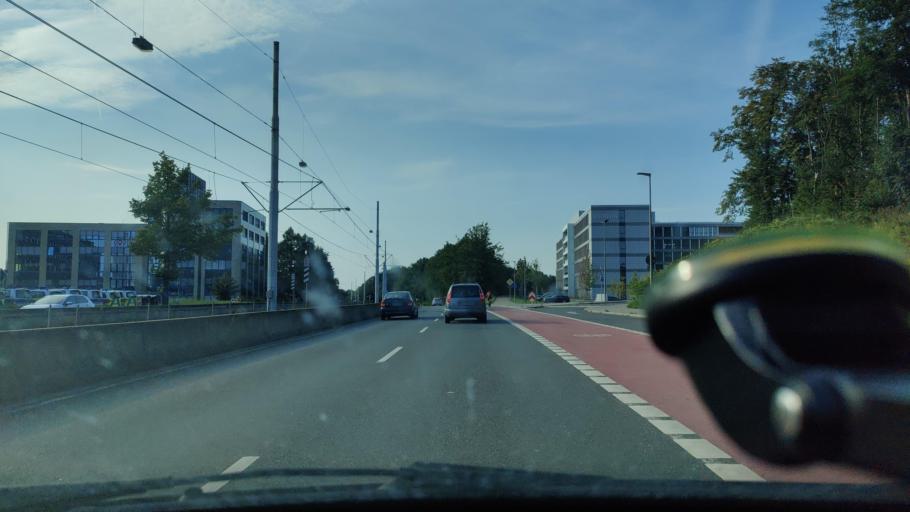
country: DE
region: North Rhine-Westphalia
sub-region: Regierungsbezirk Arnsberg
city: Bochum
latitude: 51.4610
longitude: 7.2354
